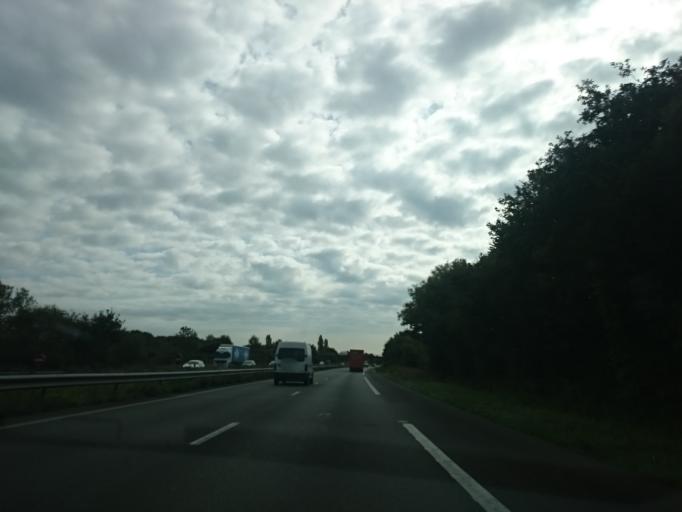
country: FR
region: Pays de la Loire
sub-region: Departement de la Loire-Atlantique
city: Le Temple-de-Bretagne
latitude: 47.3355
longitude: -1.7988
